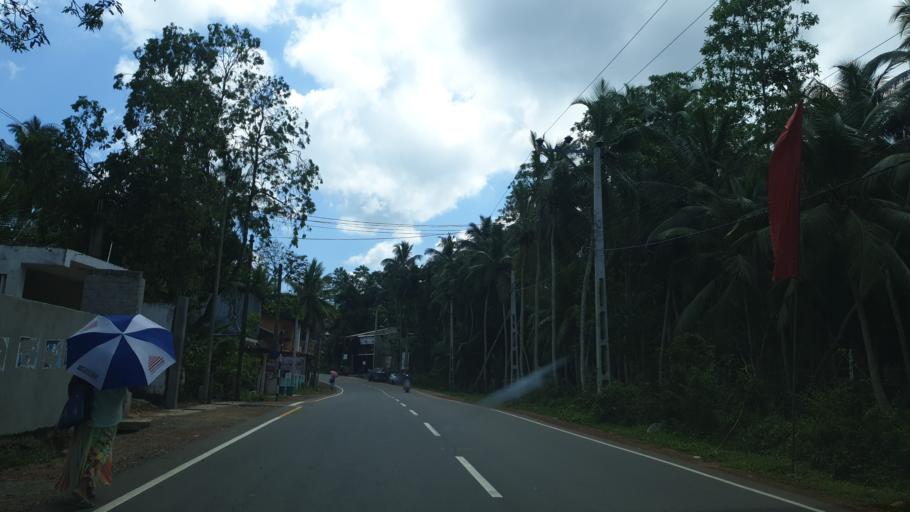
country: LK
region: Western
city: Panadura
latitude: 6.6658
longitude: 79.9497
